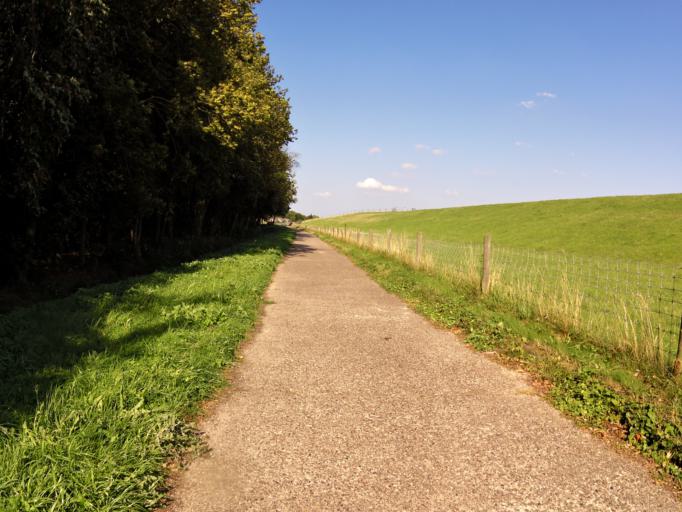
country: DE
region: Lower Saxony
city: Brake (Unterweser)
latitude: 53.4031
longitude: 8.4640
